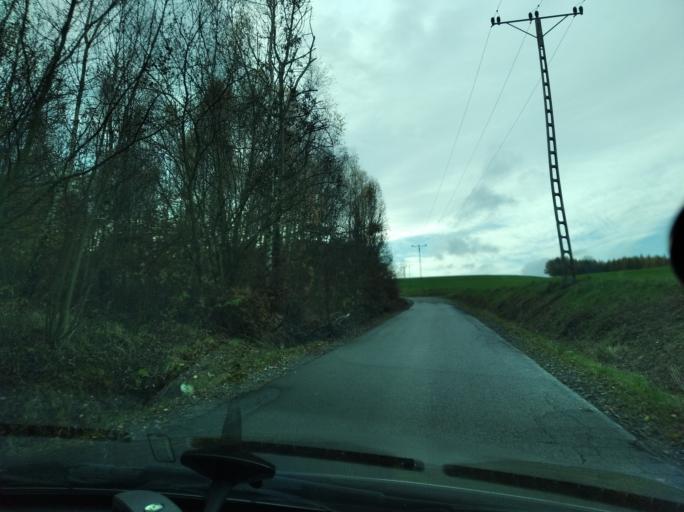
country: PL
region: Subcarpathian Voivodeship
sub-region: Powiat strzyzowski
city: Strzyzow
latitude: 49.9218
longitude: 21.7679
